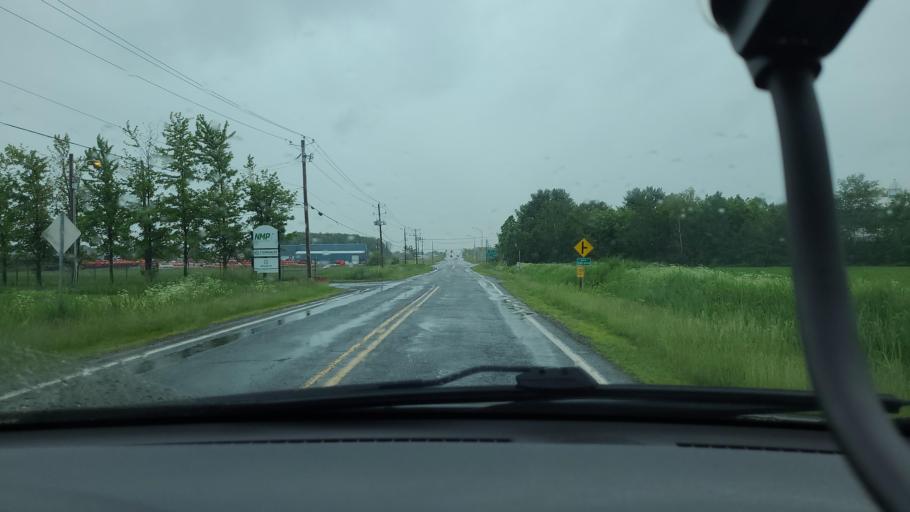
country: CA
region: Quebec
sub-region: Monteregie
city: Beloeil
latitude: 45.6124
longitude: -73.0991
